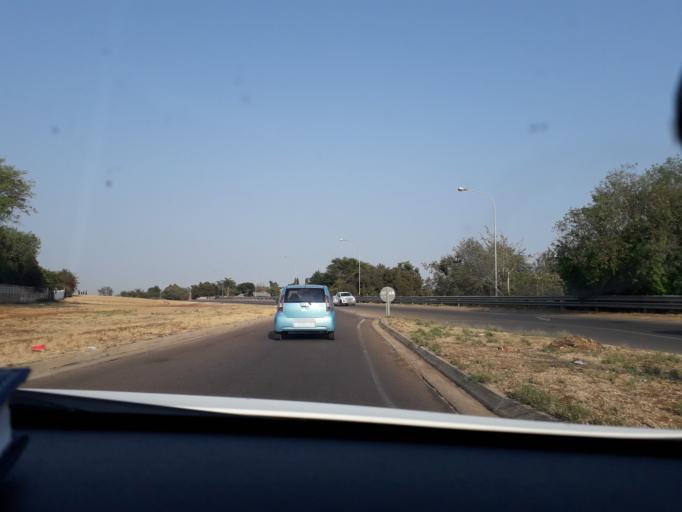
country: ZA
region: Gauteng
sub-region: City of Tshwane Metropolitan Municipality
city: Centurion
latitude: -25.8925
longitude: 28.1526
